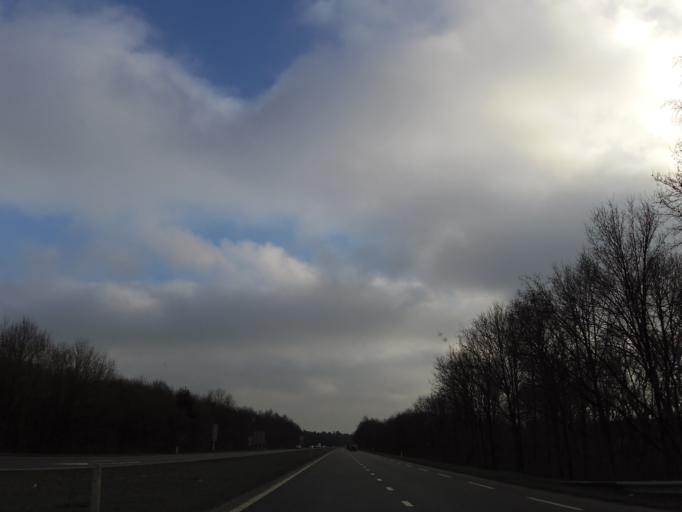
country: NL
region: Limburg
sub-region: Gemeente Gennep
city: Gennep
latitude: 51.6834
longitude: 5.9779
